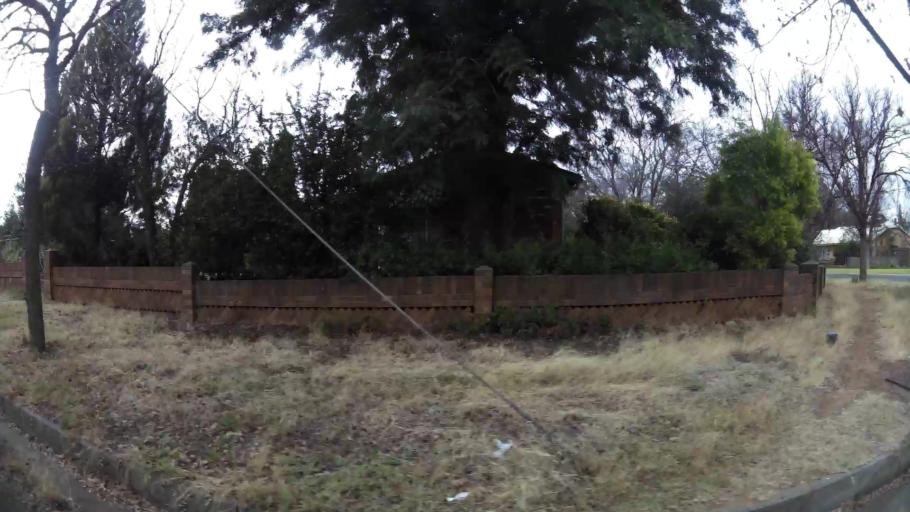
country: ZA
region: Orange Free State
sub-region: Fezile Dabi District Municipality
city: Kroonstad
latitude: -27.6346
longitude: 27.2322
